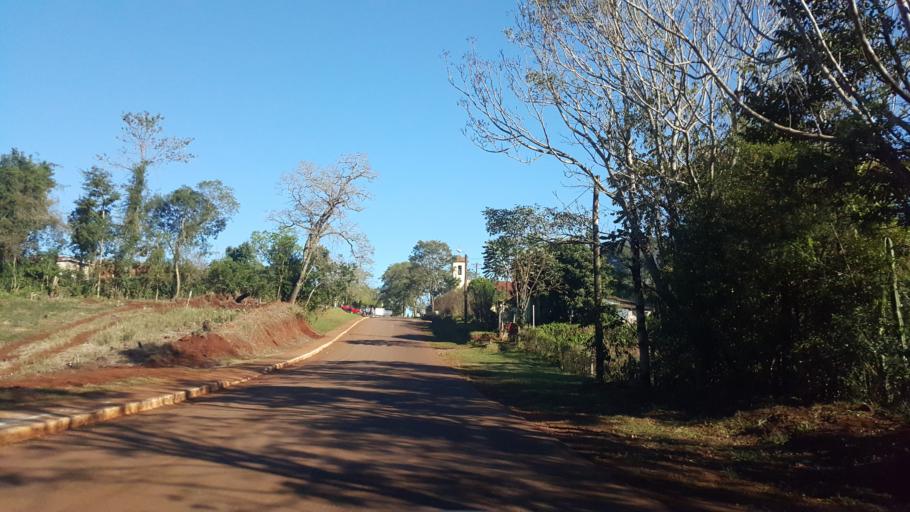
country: AR
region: Misiones
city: Jardin America
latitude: -27.0901
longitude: -55.2864
